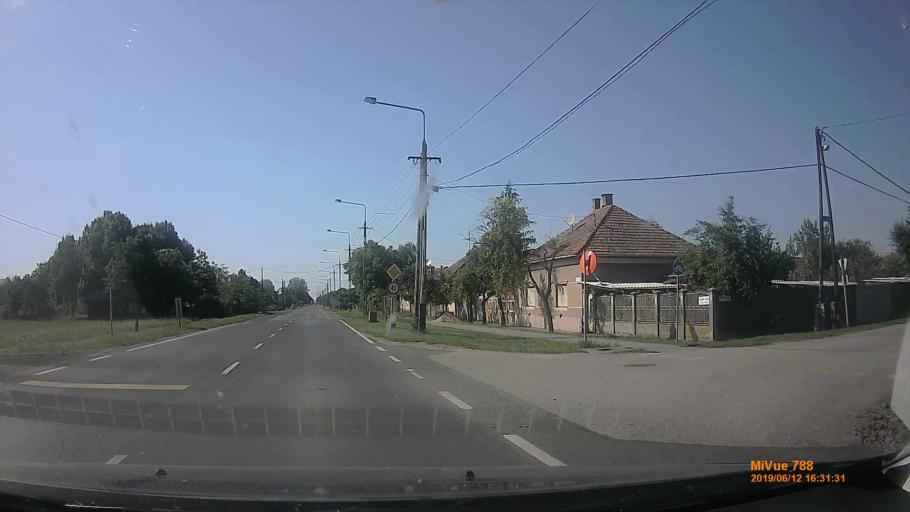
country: HU
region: Csongrad
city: Apatfalva
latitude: 46.1765
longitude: 20.5757
